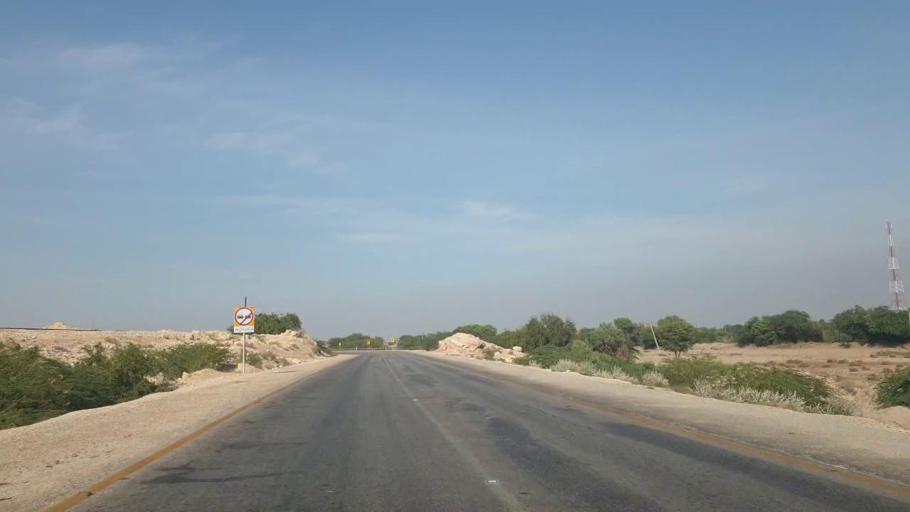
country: PK
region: Sindh
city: Sehwan
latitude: 26.2976
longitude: 67.8946
